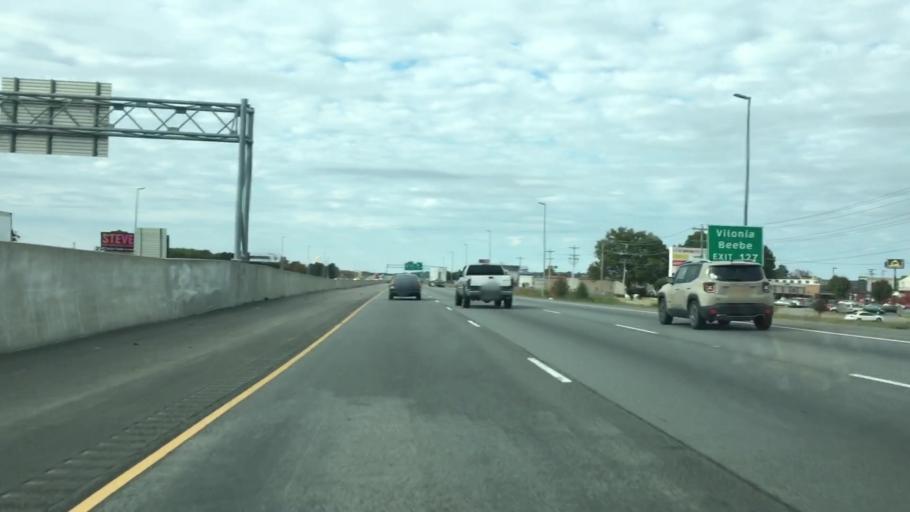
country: US
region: Arkansas
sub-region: Faulkner County
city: Conway
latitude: 35.0849
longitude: -92.4157
